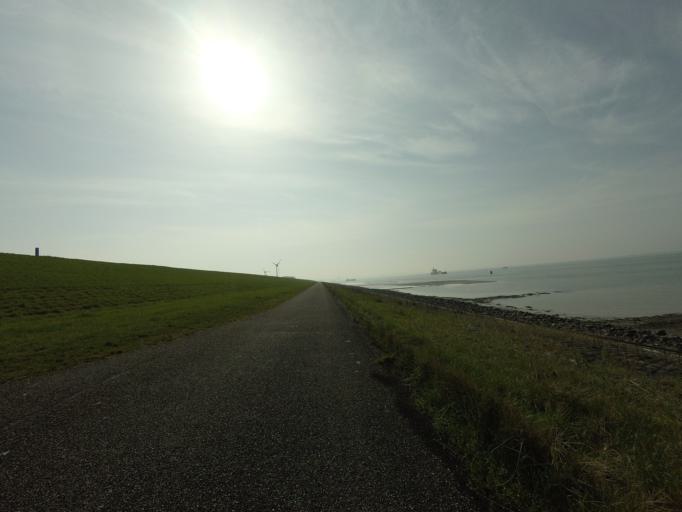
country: NL
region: Zeeland
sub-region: Gemeente Terneuzen
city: Zaamslag
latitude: 51.3609
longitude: 3.9172
